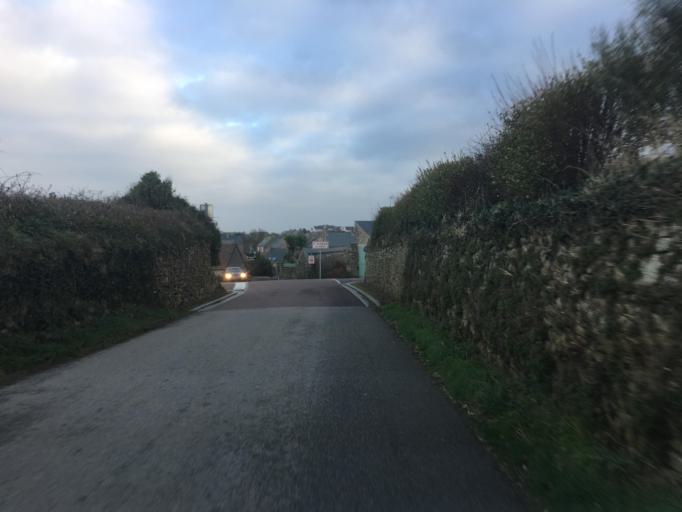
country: FR
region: Lower Normandy
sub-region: Departement de la Manche
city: Beaumont-Hague
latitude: 49.7113
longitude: -1.9244
